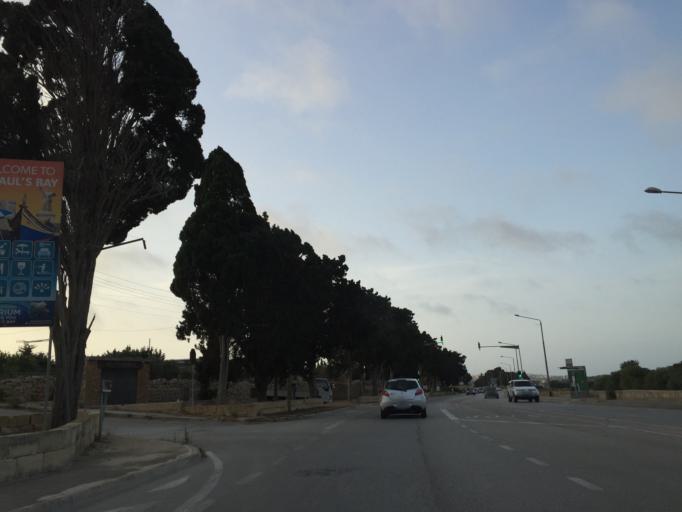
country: MT
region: Il-Mosta
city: Mosta
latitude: 35.9250
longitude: 14.4158
